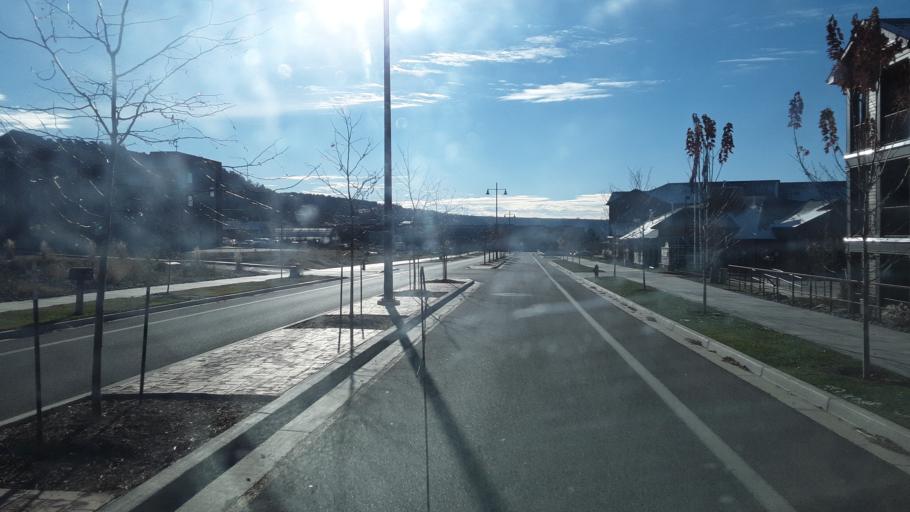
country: US
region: Colorado
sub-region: La Plata County
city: Durango
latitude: 37.2270
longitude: -107.8622
